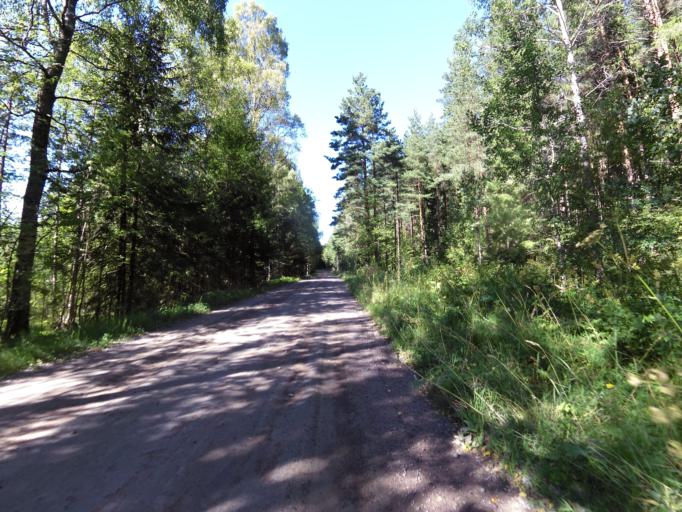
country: SE
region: Gaevleborg
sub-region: Hofors Kommun
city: Hofors
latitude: 60.5362
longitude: 16.4074
